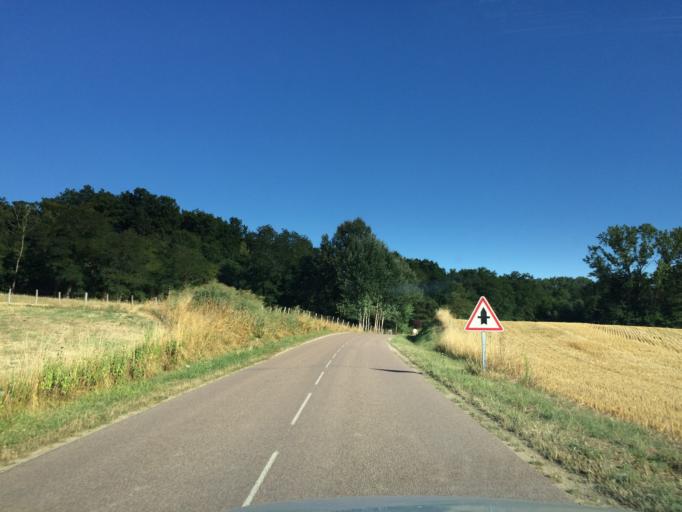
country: FR
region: Bourgogne
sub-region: Departement de l'Yonne
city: Fleury-la-Vallee
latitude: 47.8882
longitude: 3.4358
